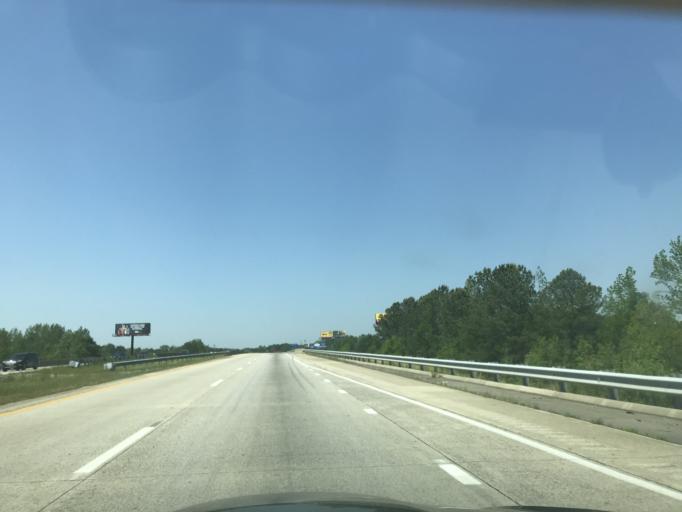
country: US
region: North Carolina
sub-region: Johnston County
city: Benson
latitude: 35.4042
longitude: -78.5233
